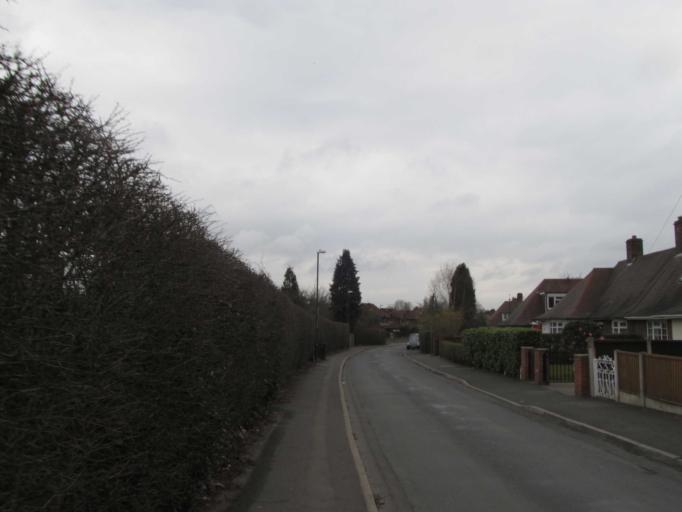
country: GB
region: England
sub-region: Nottingham
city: Nottingham
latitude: 52.9509
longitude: -1.1980
